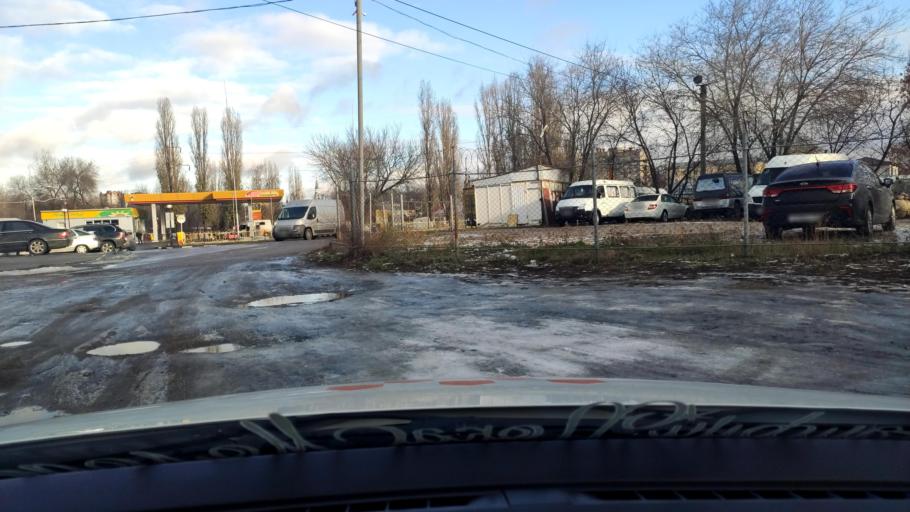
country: RU
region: Voronezj
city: Voronezh
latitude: 51.6870
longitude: 39.2051
